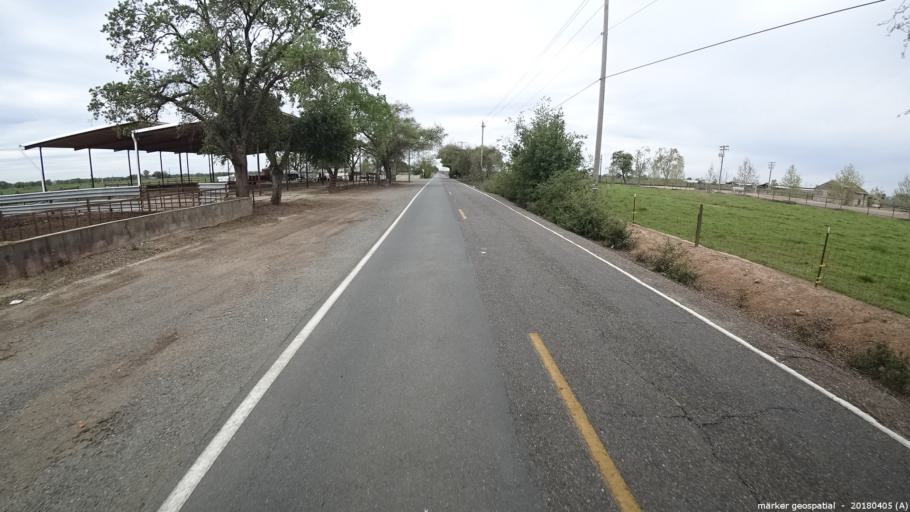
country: US
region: California
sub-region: Sacramento County
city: Galt
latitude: 38.2473
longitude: -121.3471
